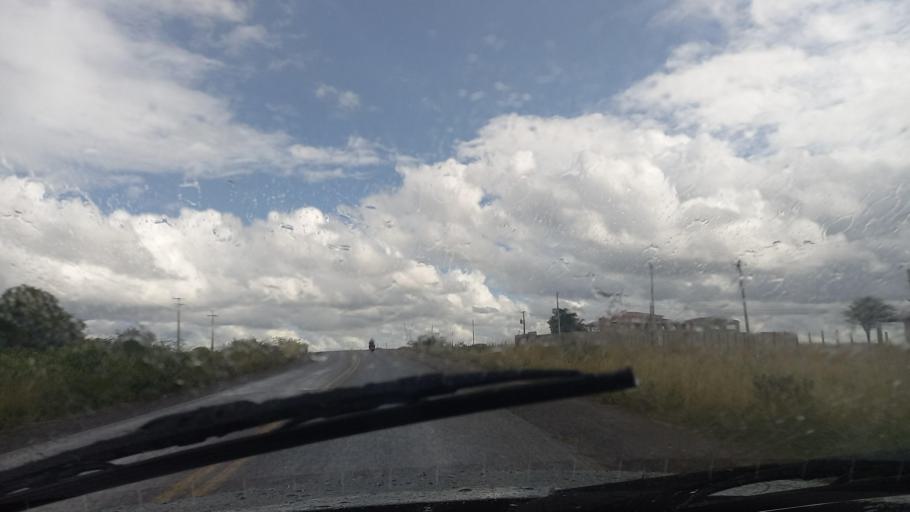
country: BR
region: Pernambuco
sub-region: Lajedo
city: Lajedo
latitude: -8.5793
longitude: -36.2872
